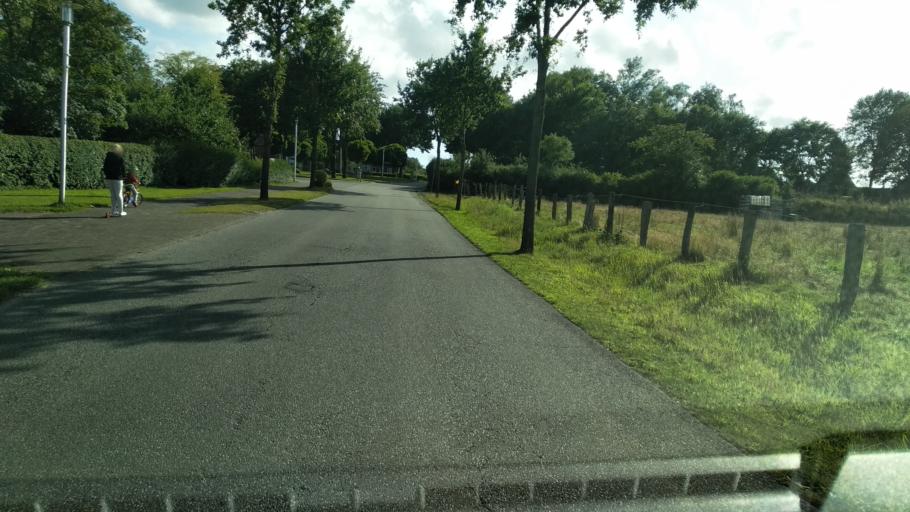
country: DE
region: Schleswig-Holstein
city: Busdorf
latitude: 54.4890
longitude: 9.5475
